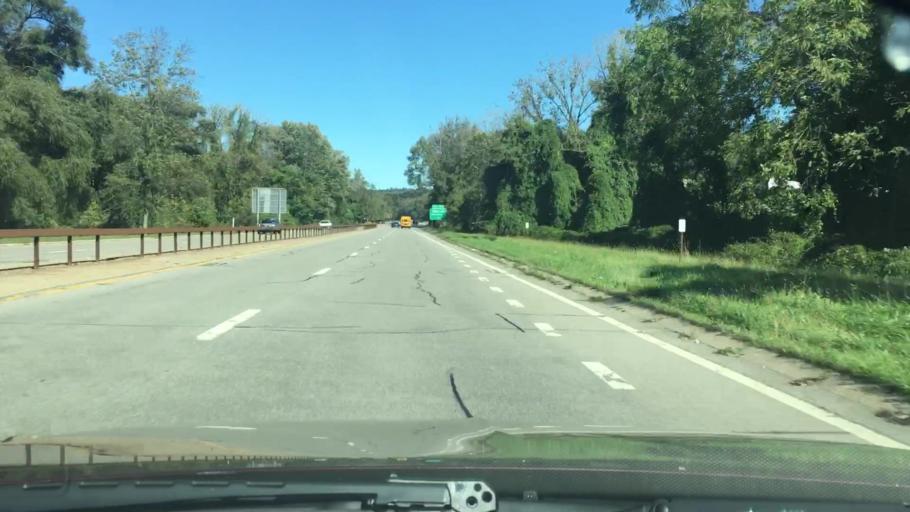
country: US
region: New York
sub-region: Westchester County
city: Hawthorne
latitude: 41.1135
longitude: -73.7940
